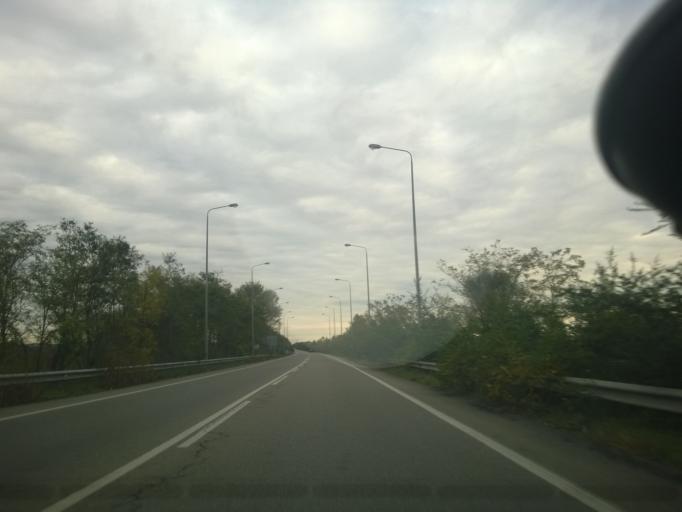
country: GR
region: Central Macedonia
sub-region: Nomos Pellis
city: Karyotissa
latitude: 40.7781
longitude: 22.3211
